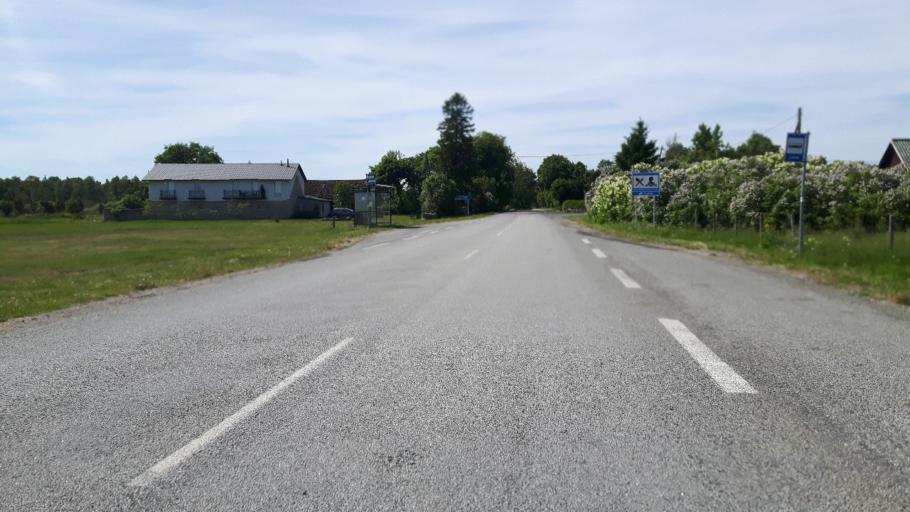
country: EE
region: Harju
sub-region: Kuusalu vald
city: Kuusalu
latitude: 59.4674
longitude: 25.3158
